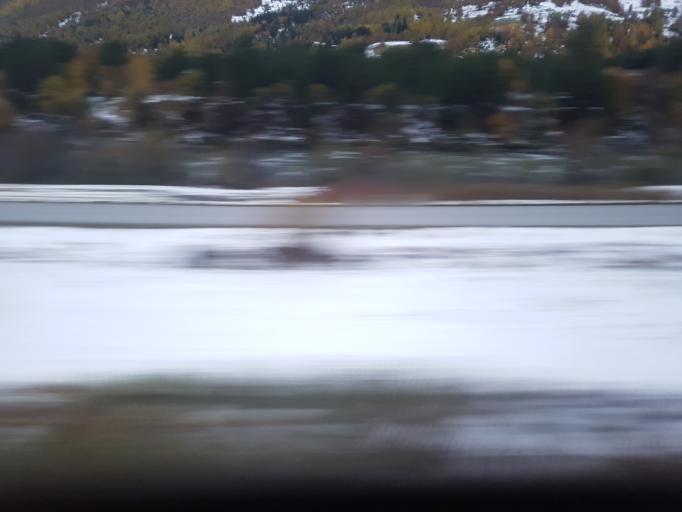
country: NO
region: Sor-Trondelag
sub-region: Oppdal
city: Oppdal
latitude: 62.5154
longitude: 9.6044
